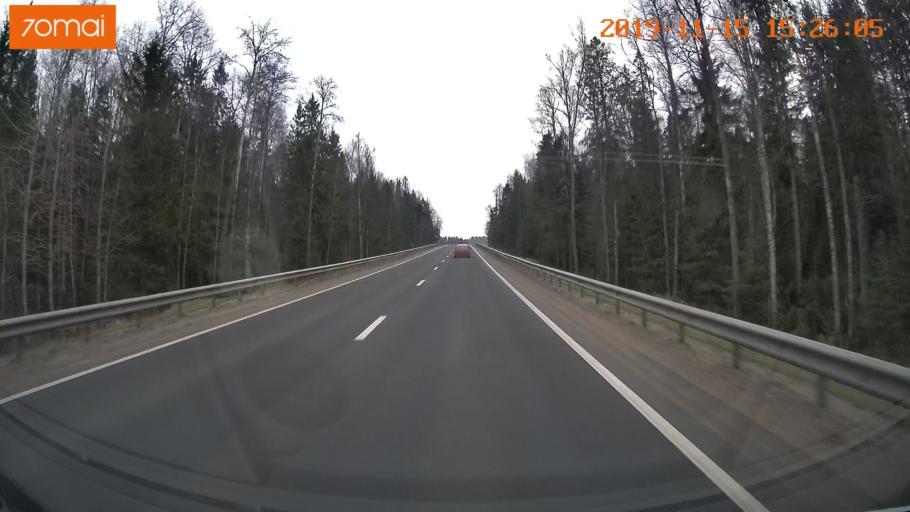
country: RU
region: Jaroslavl
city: Danilov
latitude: 58.1564
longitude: 40.1446
